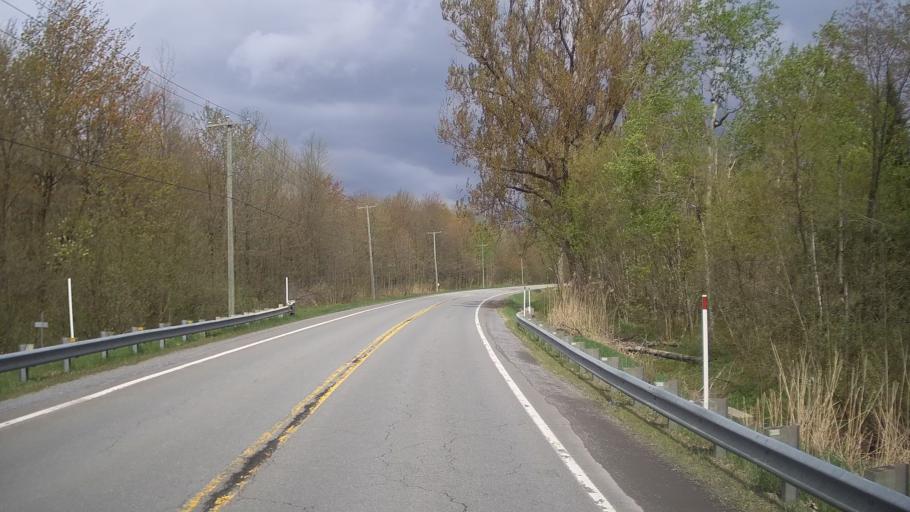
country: CA
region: Quebec
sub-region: Monteregie
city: Farnham
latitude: 45.2345
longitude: -72.8764
